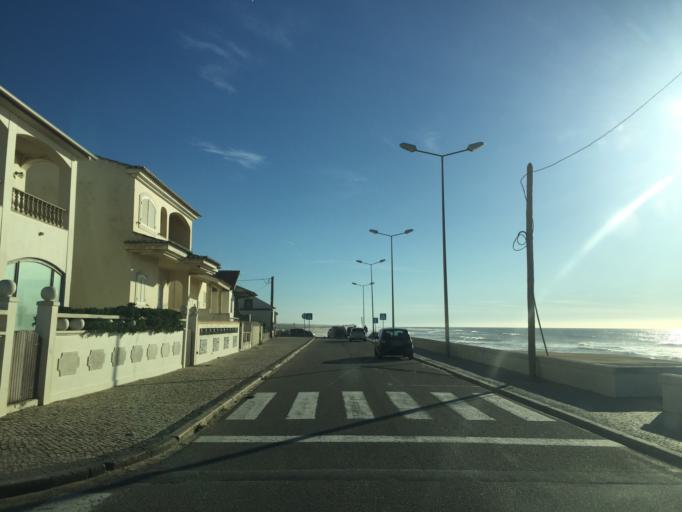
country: PT
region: Coimbra
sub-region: Figueira da Foz
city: Lavos
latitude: 40.0908
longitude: -8.8760
